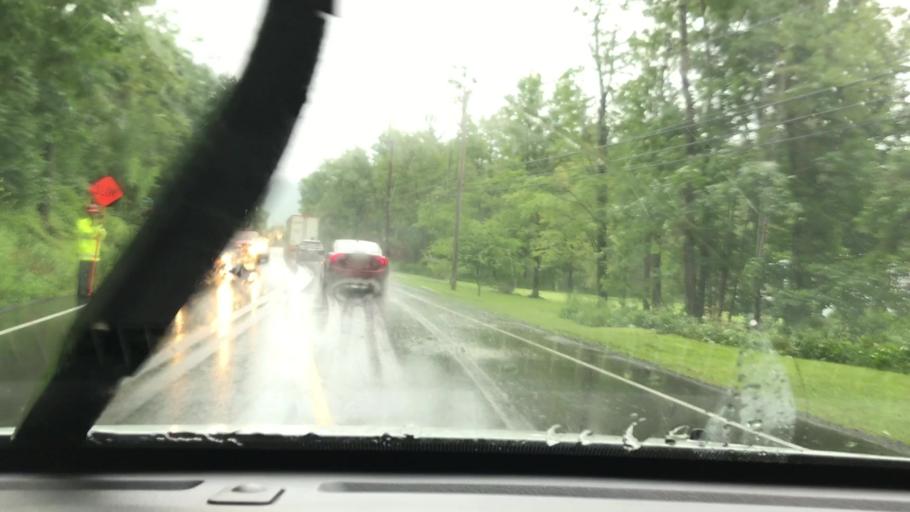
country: US
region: Pennsylvania
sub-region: Blair County
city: Tyrone
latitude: 40.7390
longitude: -78.1964
